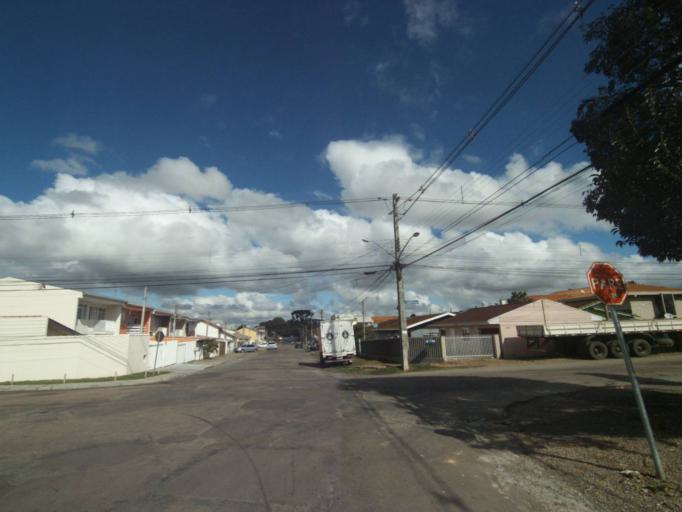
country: BR
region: Parana
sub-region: Sao Jose Dos Pinhais
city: Sao Jose dos Pinhais
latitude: -25.5376
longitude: -49.2938
